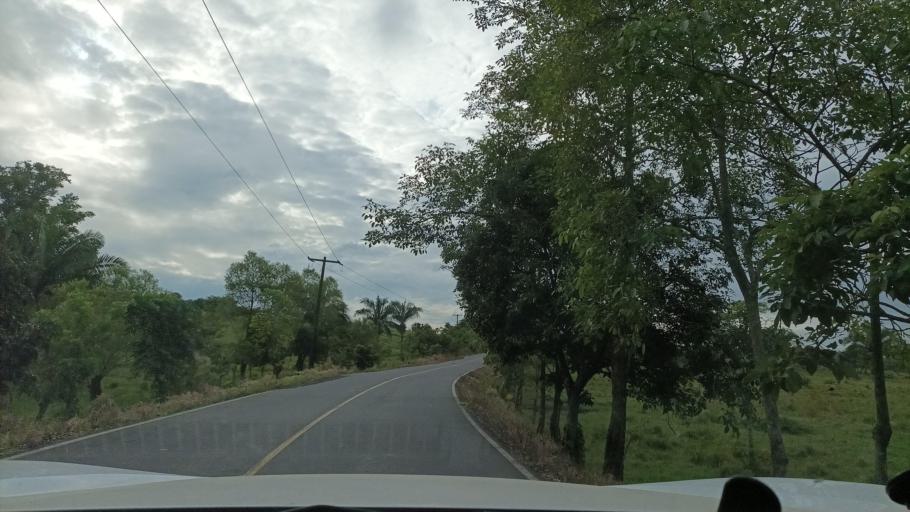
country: MX
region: Veracruz
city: Hidalgotitlan
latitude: 17.7470
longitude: -94.4933
